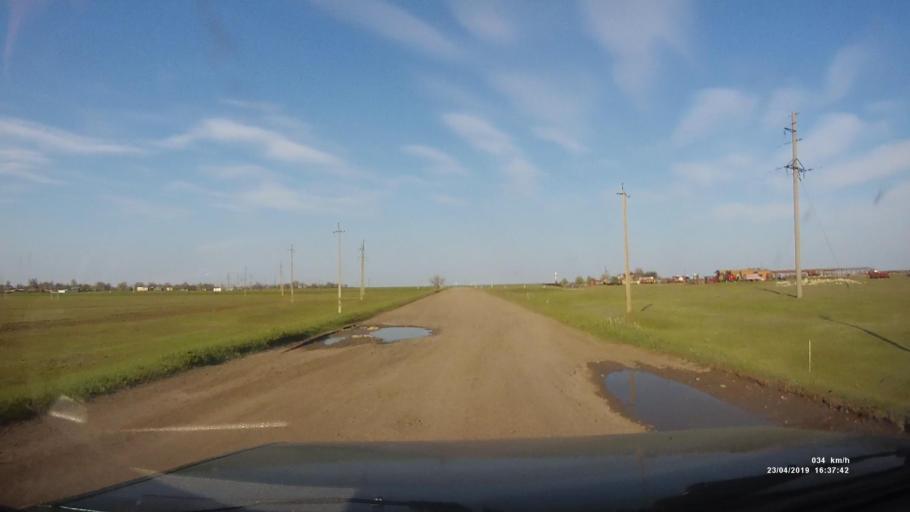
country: RU
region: Kalmykiya
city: Priyutnoye
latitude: 46.3332
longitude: 43.1486
